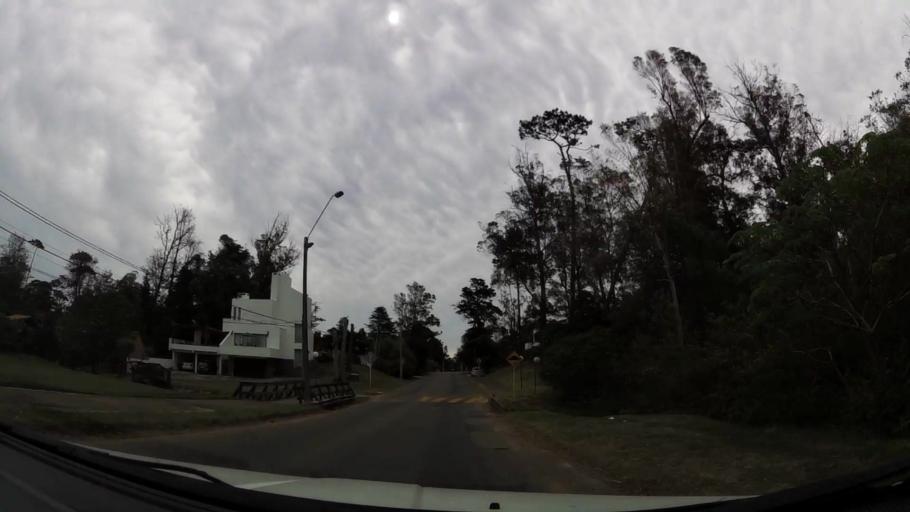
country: UY
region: Maldonado
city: Maldonado
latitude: -34.9103
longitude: -54.9823
